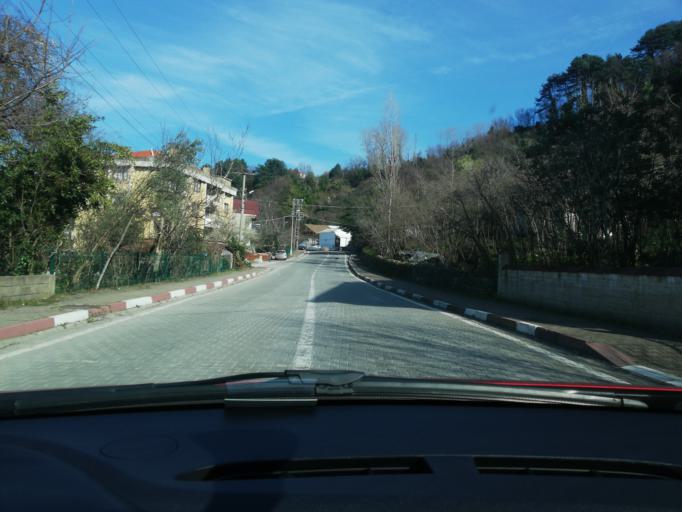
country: TR
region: Bartin
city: Kurucasile
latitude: 41.8431
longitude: 32.7283
